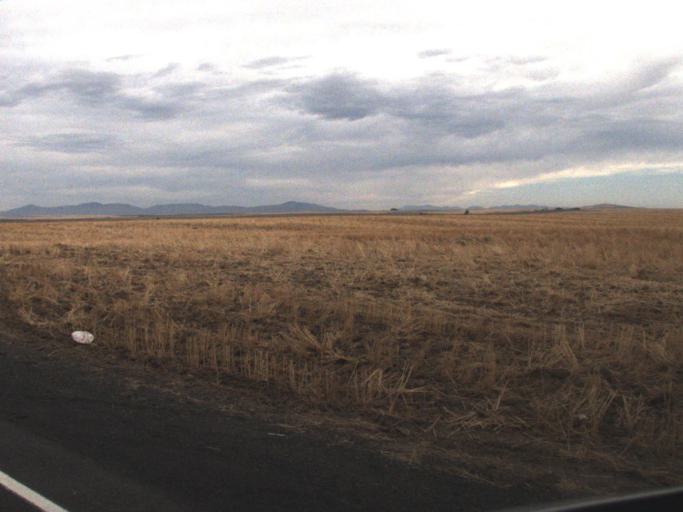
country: US
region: Washington
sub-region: Okanogan County
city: Coulee Dam
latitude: 47.6421
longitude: -118.7210
